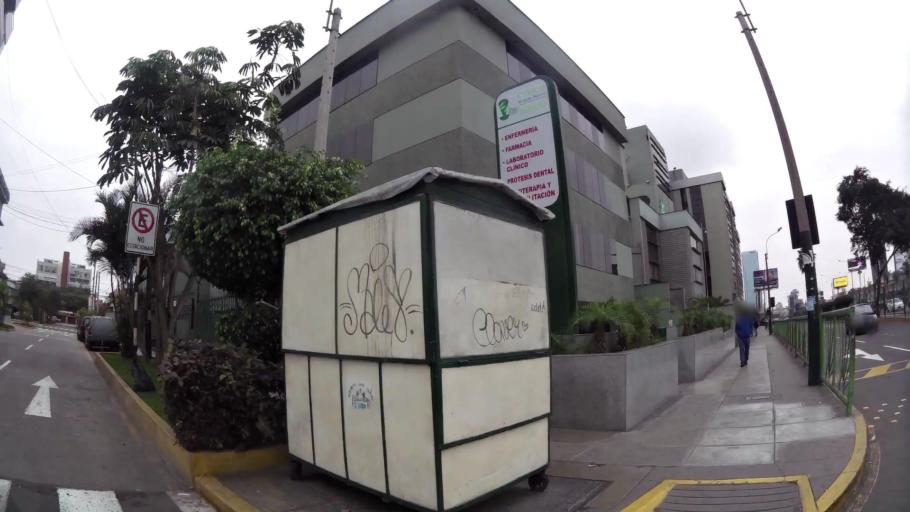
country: PE
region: Lima
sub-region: Lima
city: San Luis
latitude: -12.0904
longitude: -77.0177
